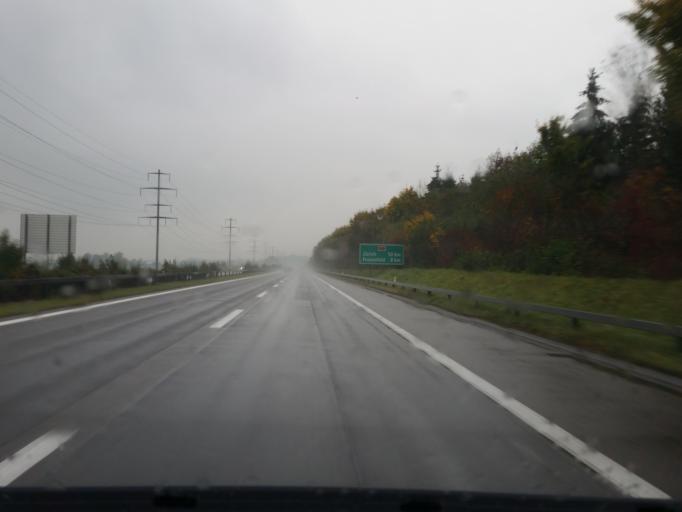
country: CH
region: Thurgau
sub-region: Frauenfeld District
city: Pfyn
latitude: 47.5880
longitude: 8.9774
